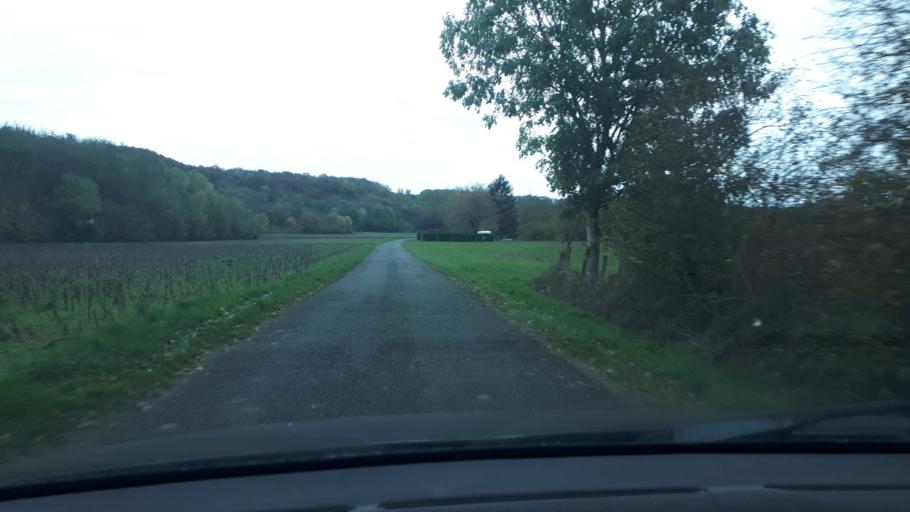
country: FR
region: Centre
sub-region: Departement du Loir-et-Cher
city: Lunay
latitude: 47.7699
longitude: 0.9502
